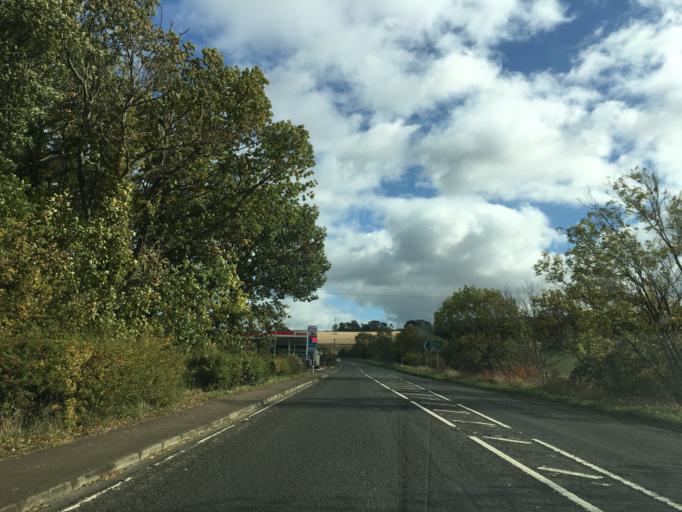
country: GB
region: Scotland
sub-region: Midlothian
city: Dalkeith
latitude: 55.8900
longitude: -3.0272
